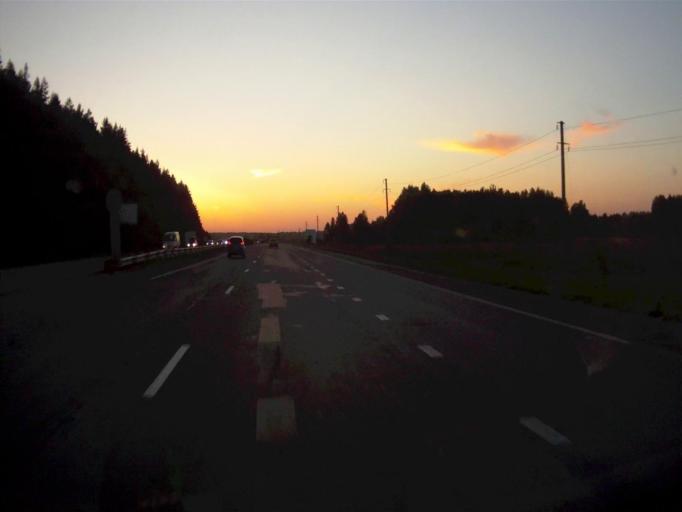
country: RU
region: Chelyabinsk
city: Roshchino
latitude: 55.1928
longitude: 61.2196
